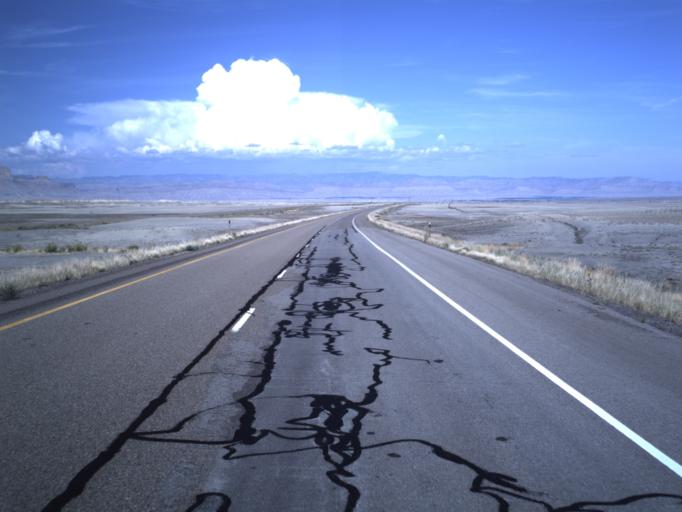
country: US
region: Utah
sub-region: Carbon County
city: East Carbon City
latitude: 38.9490
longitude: -110.3186
